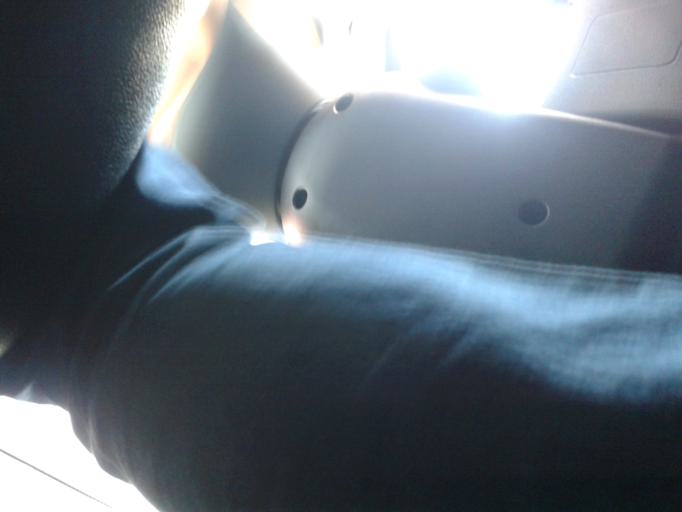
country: BR
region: Minas Gerais
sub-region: Ituiutaba
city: Ituiutaba
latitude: -19.0794
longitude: -49.7500
